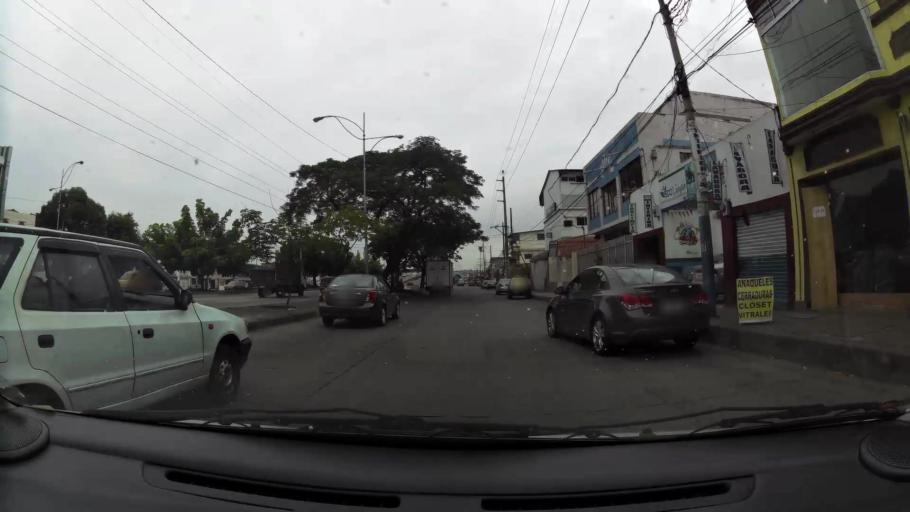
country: EC
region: Guayas
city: Eloy Alfaro
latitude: -2.1409
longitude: -79.9040
